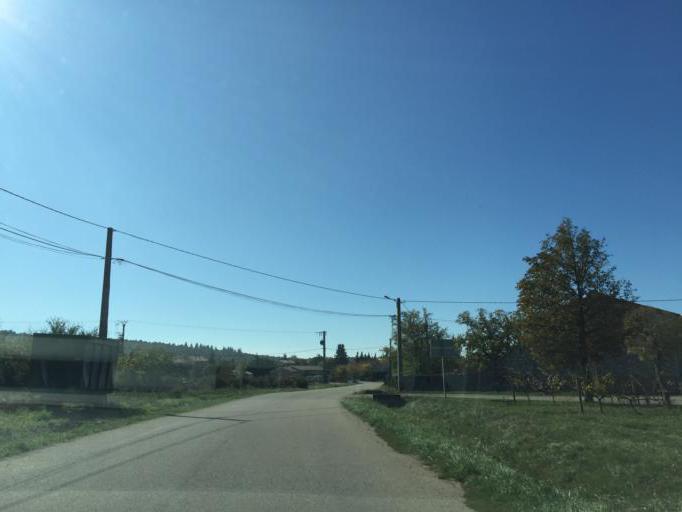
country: FR
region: Languedoc-Roussillon
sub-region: Departement du Gard
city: Saint-Julien-de-Peyrolas
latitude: 44.3955
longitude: 4.5064
